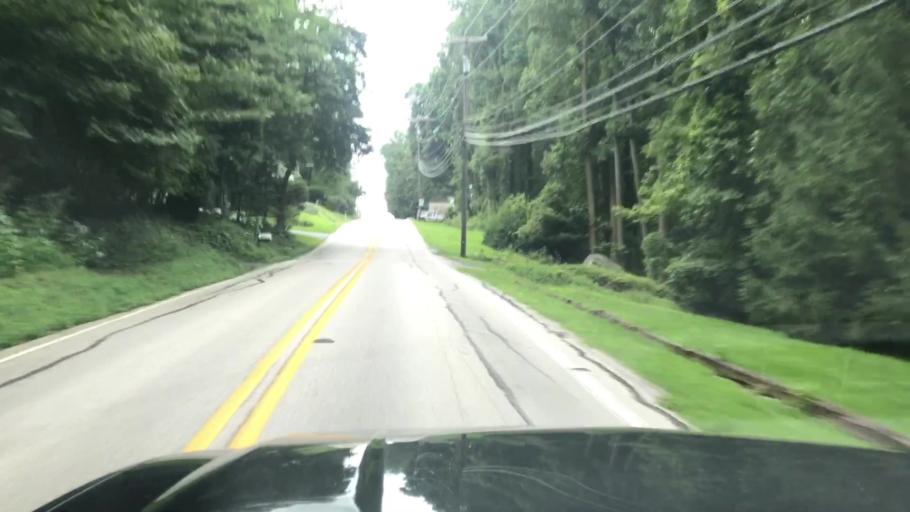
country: US
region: Pennsylvania
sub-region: Cumberland County
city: New Cumberland
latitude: 40.1842
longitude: -76.8689
